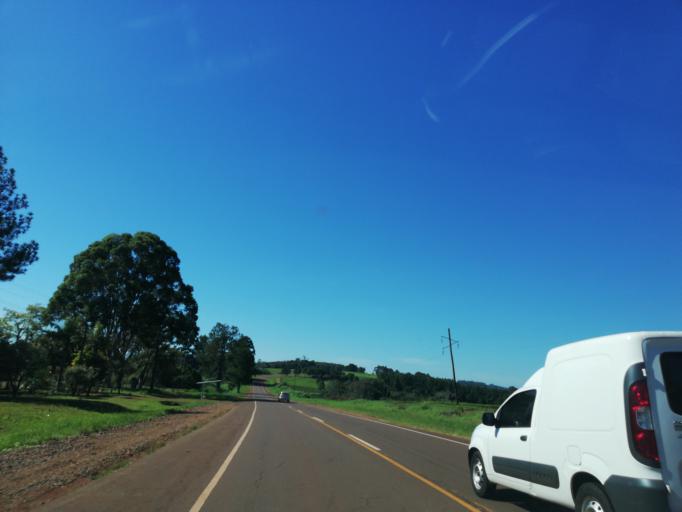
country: AR
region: Misiones
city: Dos de Mayo
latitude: -27.0628
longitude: -54.4252
